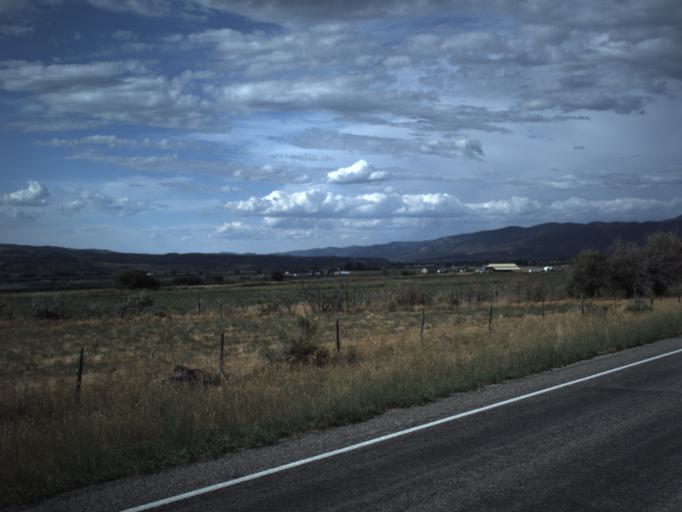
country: US
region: Utah
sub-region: Sanpete County
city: Mount Pleasant
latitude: 39.5149
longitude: -111.4904
